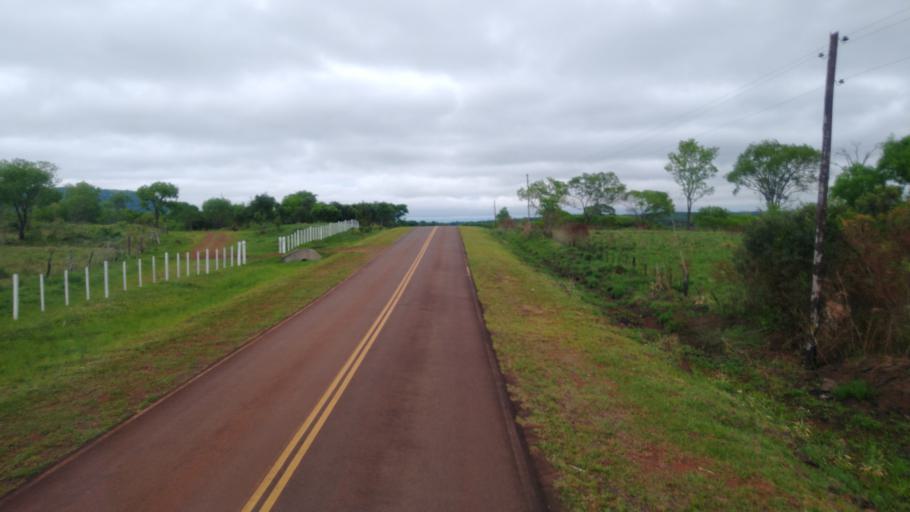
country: AR
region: Misiones
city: Santa Ana
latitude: -27.4106
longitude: -55.5569
